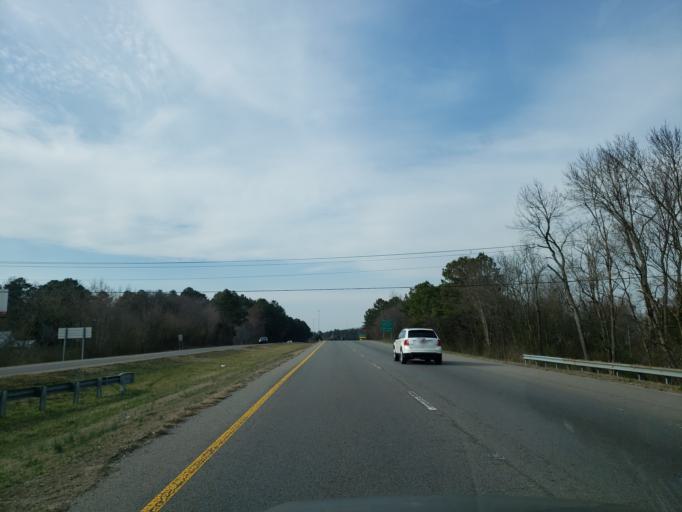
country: US
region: Tennessee
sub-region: Bradley County
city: East Cleveland
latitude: 35.1602
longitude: -84.8454
